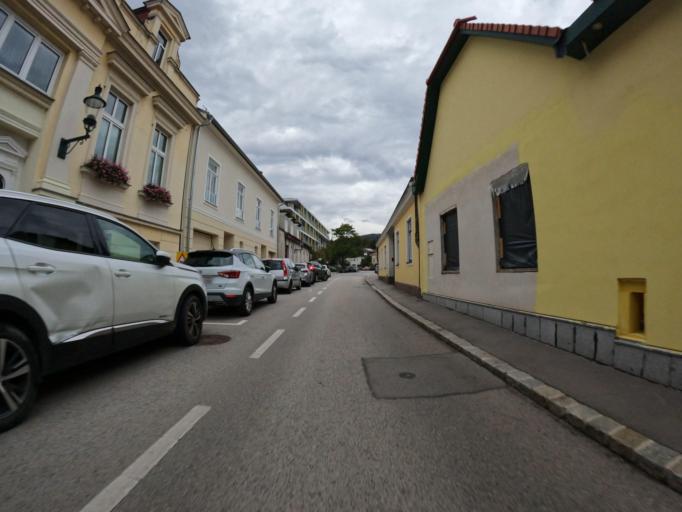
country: AT
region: Lower Austria
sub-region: Politischer Bezirk Baden
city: Baden
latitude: 48.0100
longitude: 16.2409
